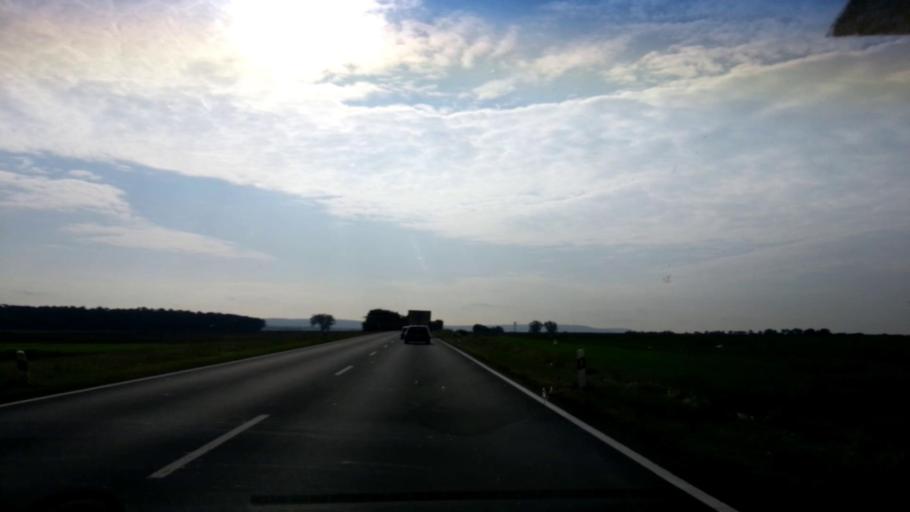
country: DE
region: Bavaria
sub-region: Regierungsbezirk Unterfranken
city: Prichsenstadt
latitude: 49.8282
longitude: 10.3560
